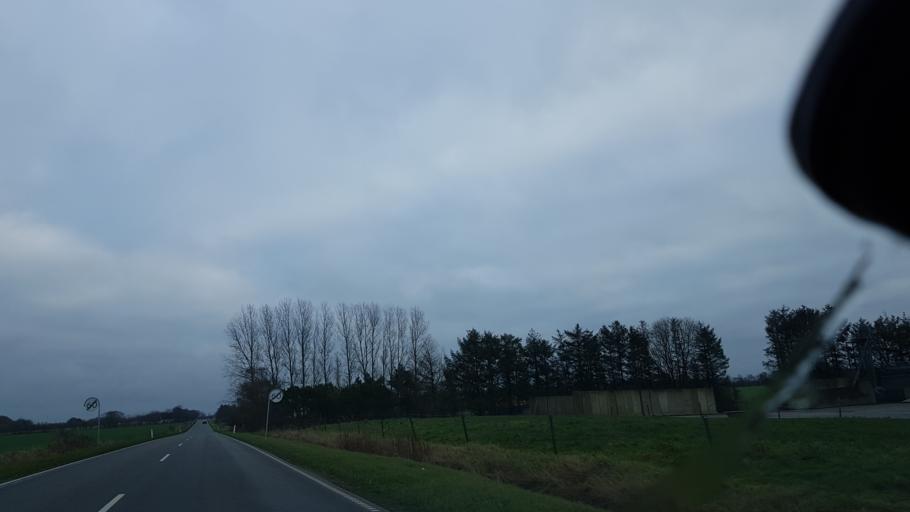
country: DK
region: South Denmark
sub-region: Tonder Kommune
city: Toftlund
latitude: 55.1931
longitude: 9.0868
